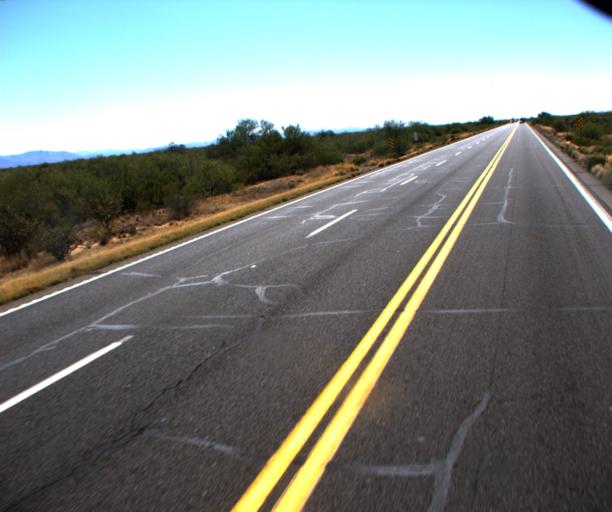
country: US
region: Arizona
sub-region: Yavapai County
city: Congress
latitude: 34.1351
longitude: -112.9674
